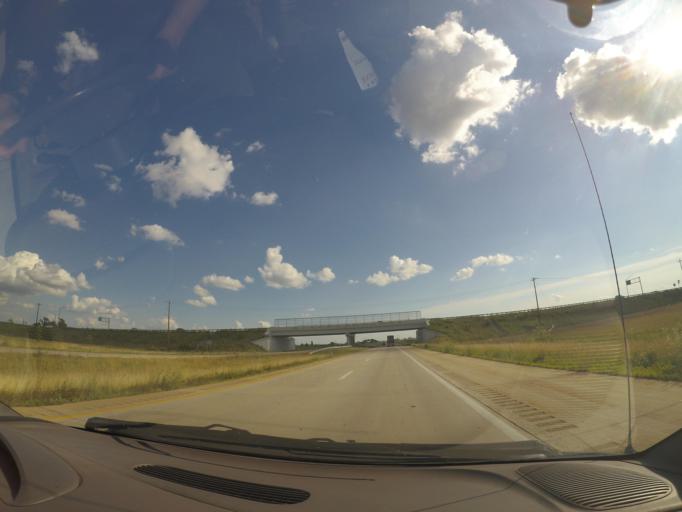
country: US
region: Ohio
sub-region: Lucas County
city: Waterville
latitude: 41.5095
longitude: -83.7538
